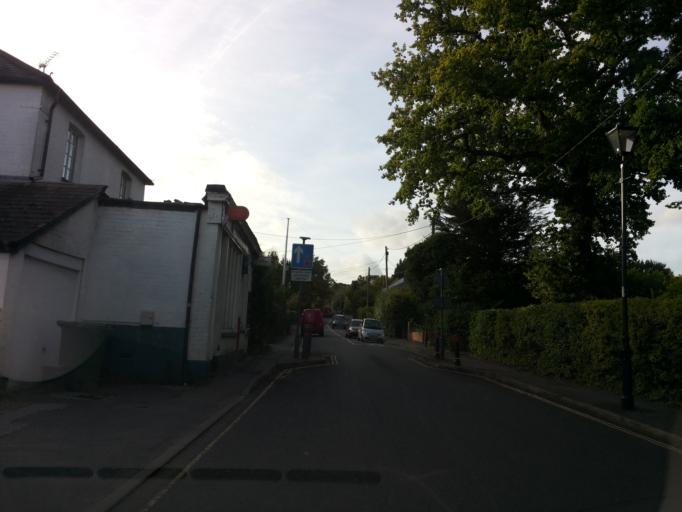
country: GB
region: England
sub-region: Surrey
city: Windlesham
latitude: 51.3647
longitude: -0.6544
